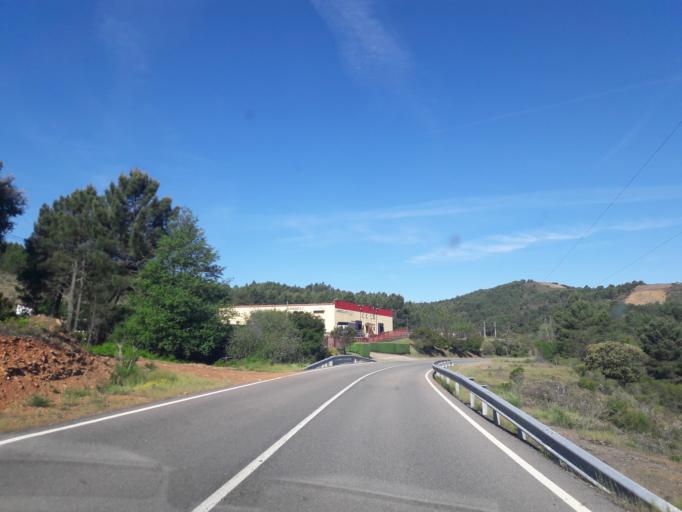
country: ES
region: Castille and Leon
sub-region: Provincia de Salamanca
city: Herguijuela de la Sierra
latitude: 40.4139
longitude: -6.1157
